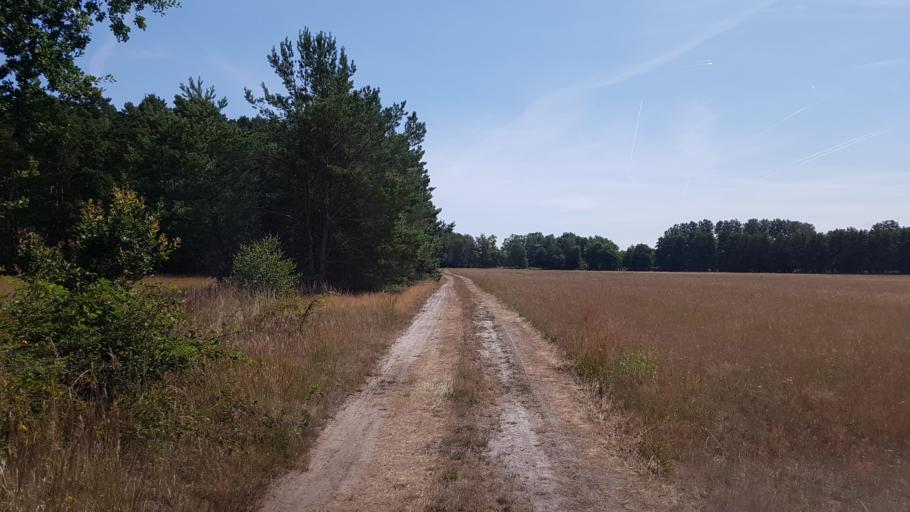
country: DE
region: Brandenburg
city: Crinitz
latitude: 51.6621
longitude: 13.7731
